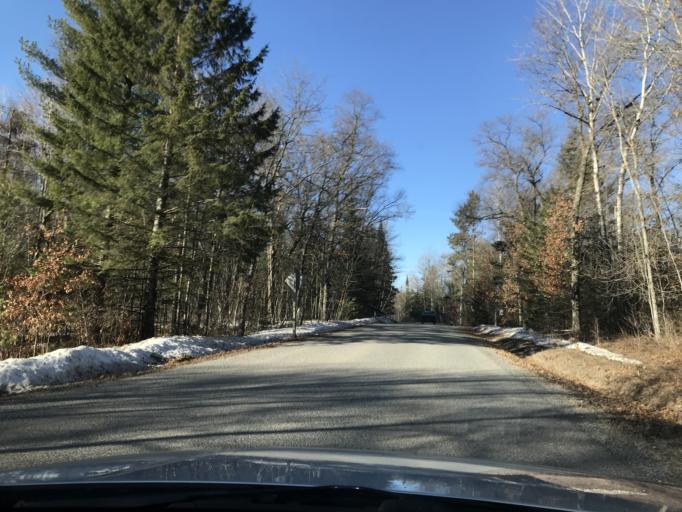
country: US
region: Wisconsin
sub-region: Marinette County
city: Niagara
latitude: 45.3916
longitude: -88.0572
